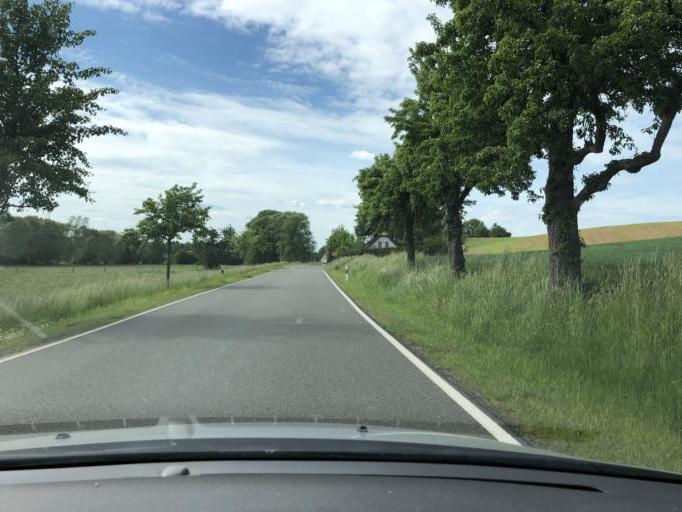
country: DE
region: Saxony
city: Nerchau
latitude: 51.2123
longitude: 12.8160
